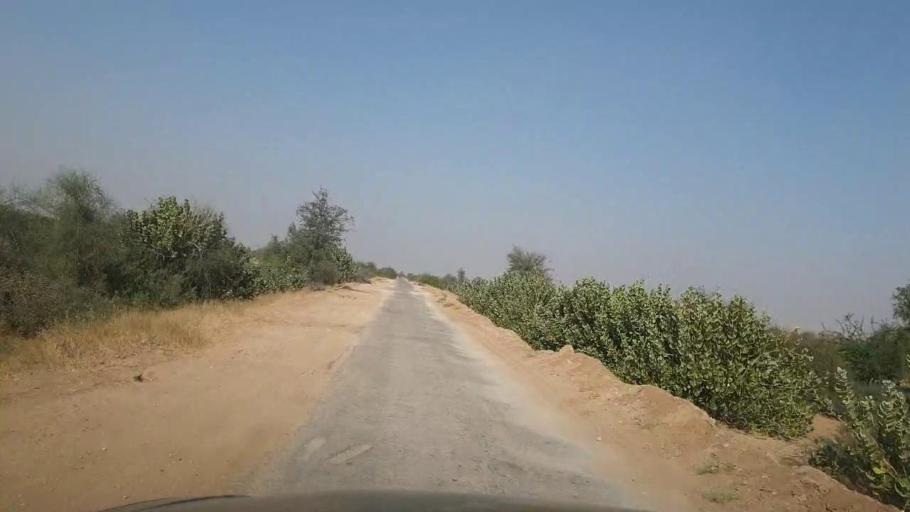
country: PK
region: Sindh
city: Jamshoro
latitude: 25.4768
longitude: 67.8219
